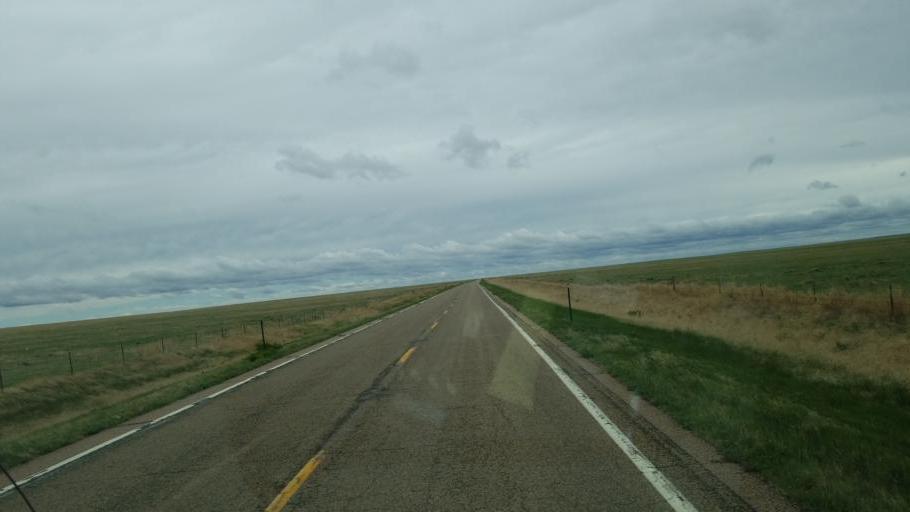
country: US
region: Colorado
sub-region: Lincoln County
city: Hugo
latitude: 38.8521
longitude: -103.7349
